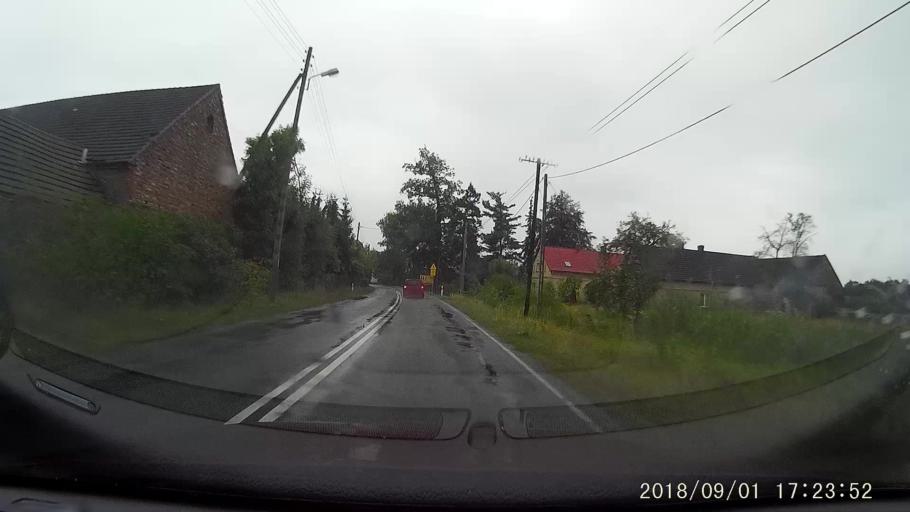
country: PL
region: Lubusz
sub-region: Powiat zaganski
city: Zagan
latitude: 51.6963
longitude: 15.2977
